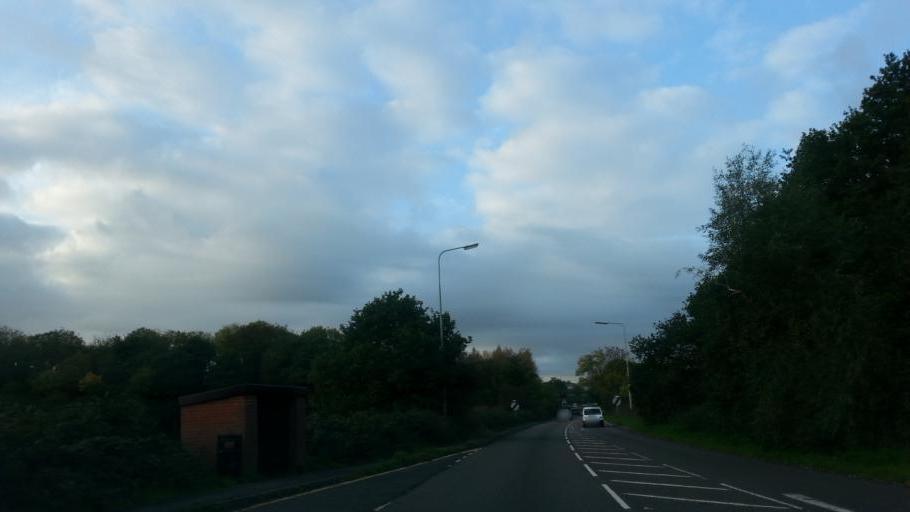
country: GB
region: England
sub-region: Staffordshire
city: Fazeley
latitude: 52.6139
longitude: -1.7410
